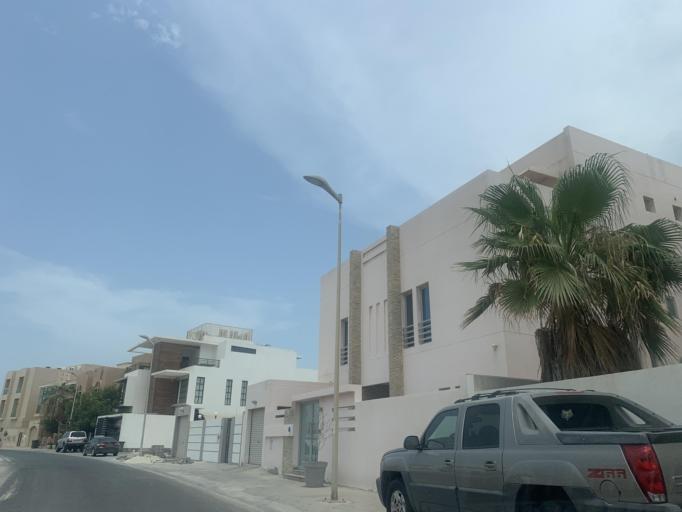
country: BH
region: Muharraq
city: Al Hadd
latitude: 26.2898
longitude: 50.6740
